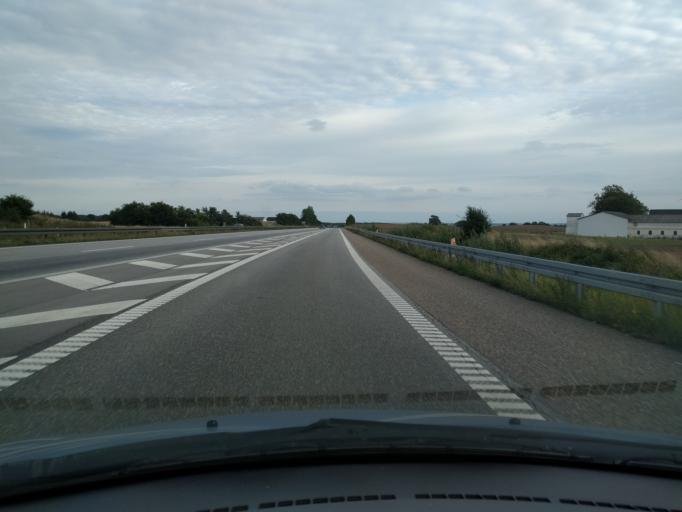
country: DK
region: Zealand
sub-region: Vordingborg Kommune
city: Nyrad
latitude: 54.9973
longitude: 11.9949
